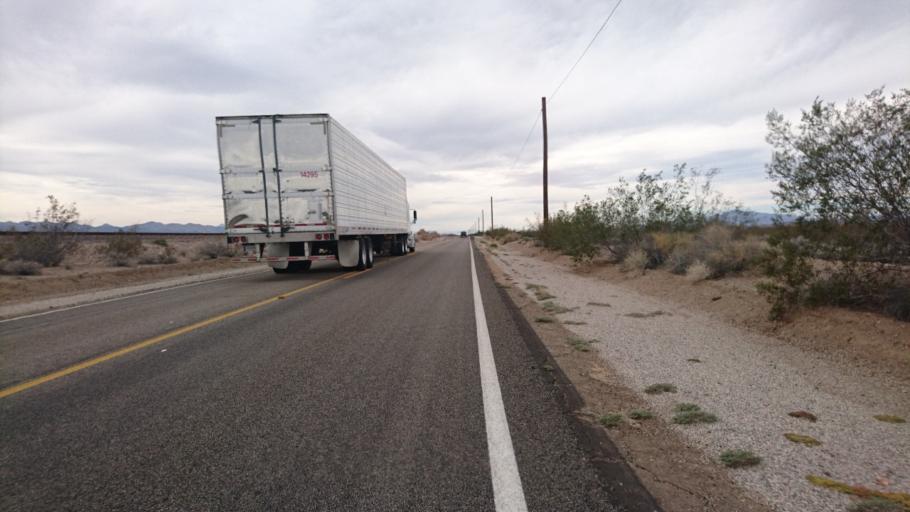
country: US
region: California
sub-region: San Bernardino County
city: Needles
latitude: 34.8860
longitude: -115.0999
